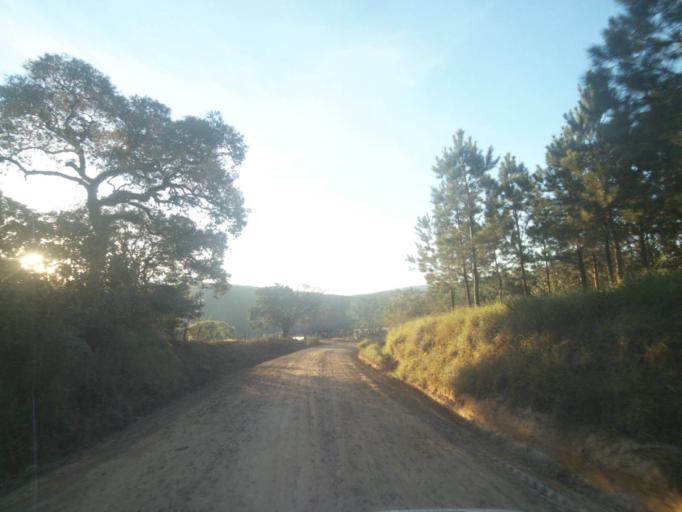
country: BR
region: Parana
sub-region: Tibagi
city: Tibagi
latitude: -24.5393
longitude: -50.5327
